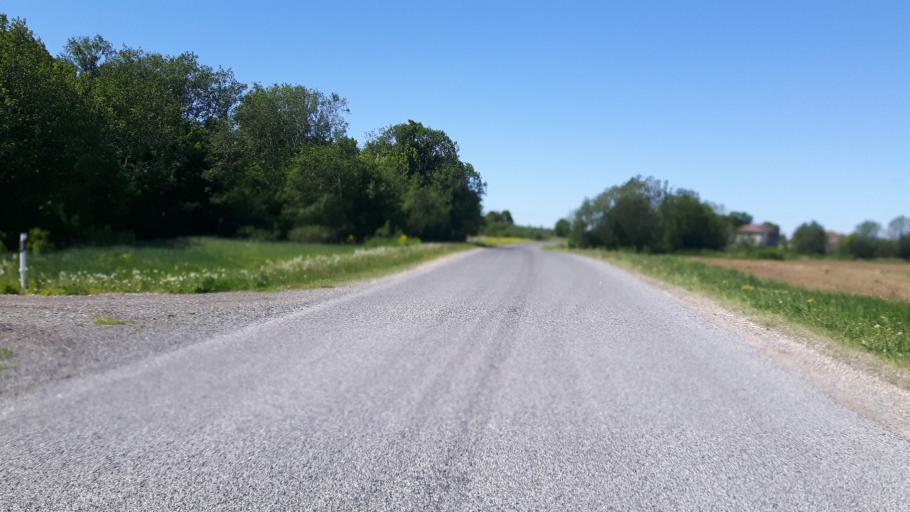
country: EE
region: Ida-Virumaa
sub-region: Sillamaee linn
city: Sillamae
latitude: 59.3823
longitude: 27.8207
